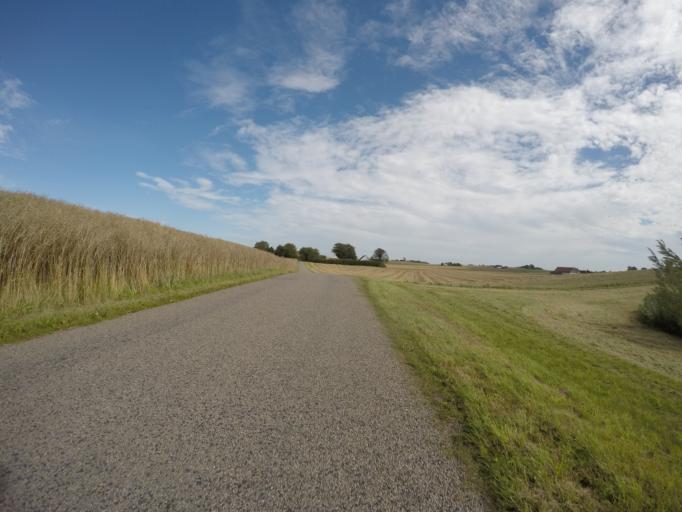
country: SE
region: Skane
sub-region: Simrishamns Kommun
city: Simrishamn
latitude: 55.4974
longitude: 14.2338
